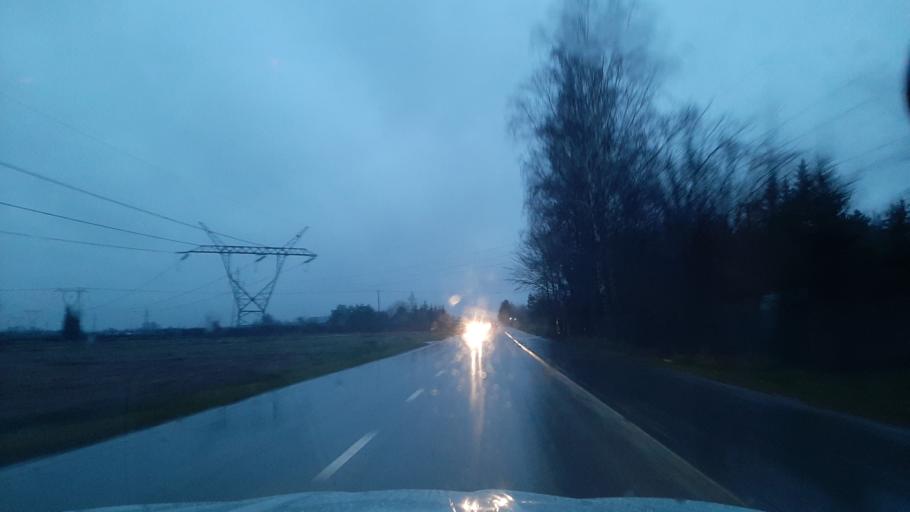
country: PL
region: Lublin Voivodeship
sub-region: Powiat lubelski
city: Jastkow
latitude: 51.3339
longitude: 22.5059
